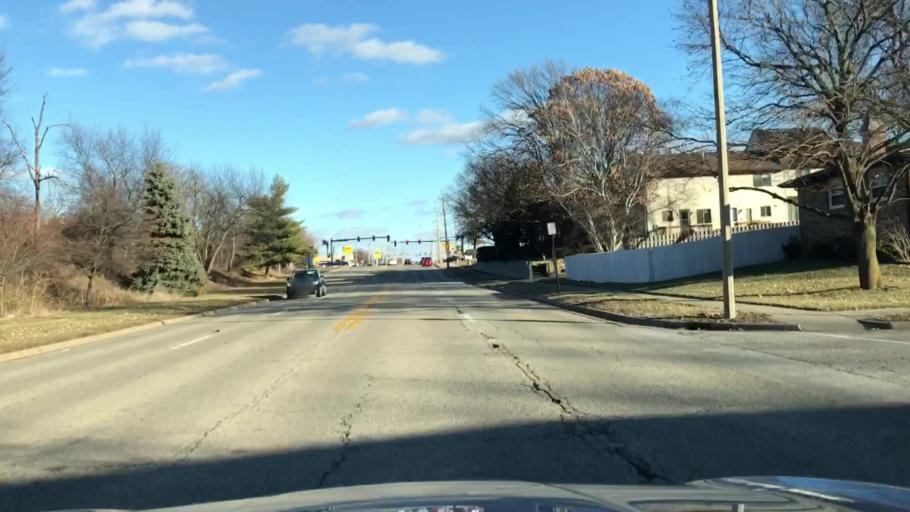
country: US
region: Illinois
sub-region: McLean County
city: Normal
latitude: 40.5027
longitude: -88.9601
